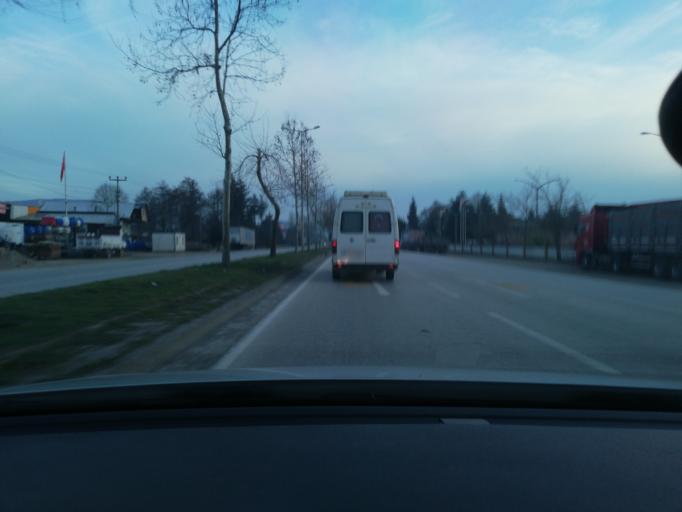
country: TR
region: Duzce
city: Duzce
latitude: 40.8731
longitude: 31.1692
